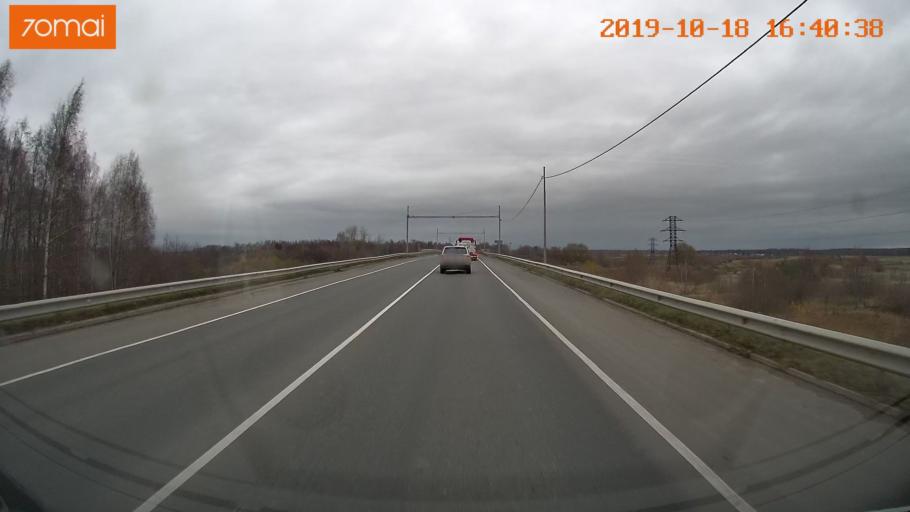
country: RU
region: Vladimir
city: Suzdal'
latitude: 56.4607
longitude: 40.4650
